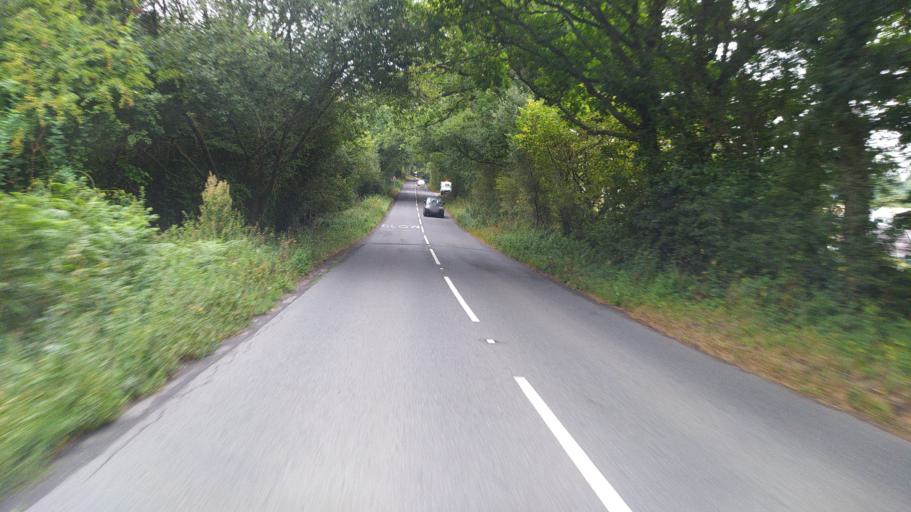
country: GB
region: England
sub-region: Dorset
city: Verwood
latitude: 50.8852
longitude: -1.9036
